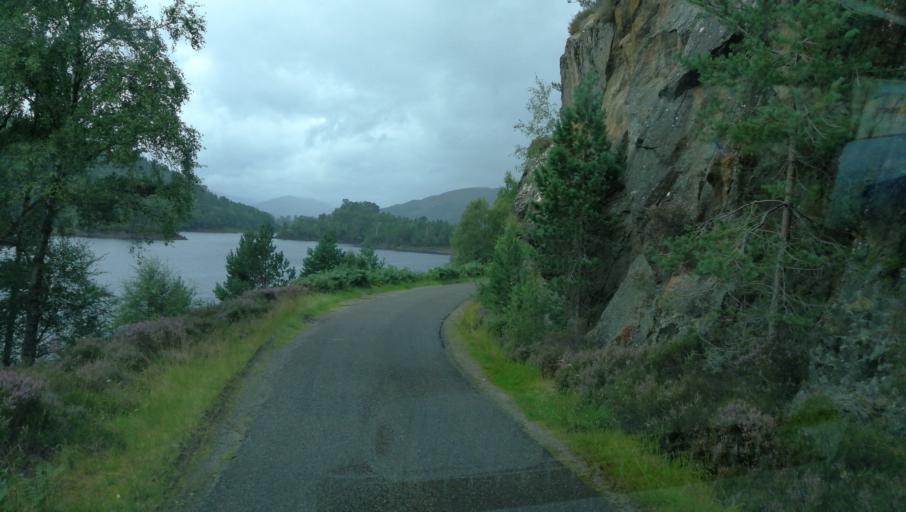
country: GB
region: Scotland
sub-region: Highland
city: Spean Bridge
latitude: 57.3021
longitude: -4.8774
